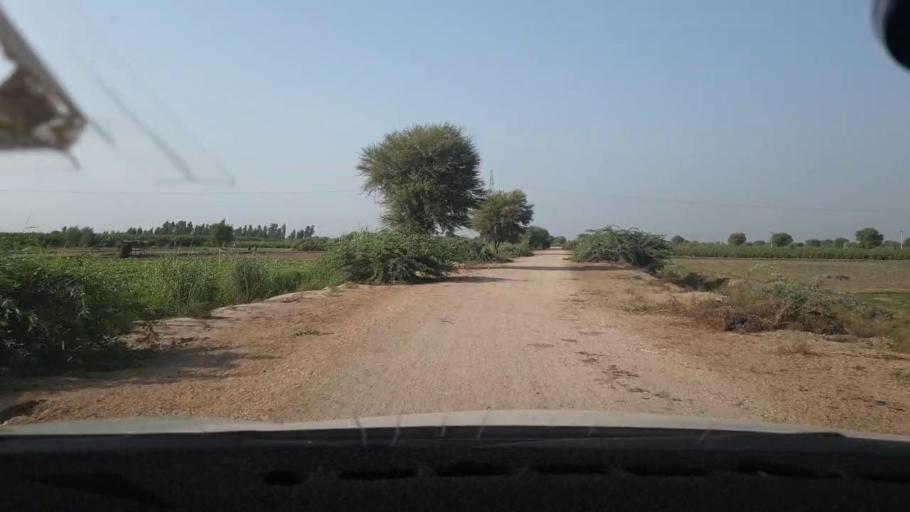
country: PK
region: Sindh
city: Berani
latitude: 25.7491
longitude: 68.7756
